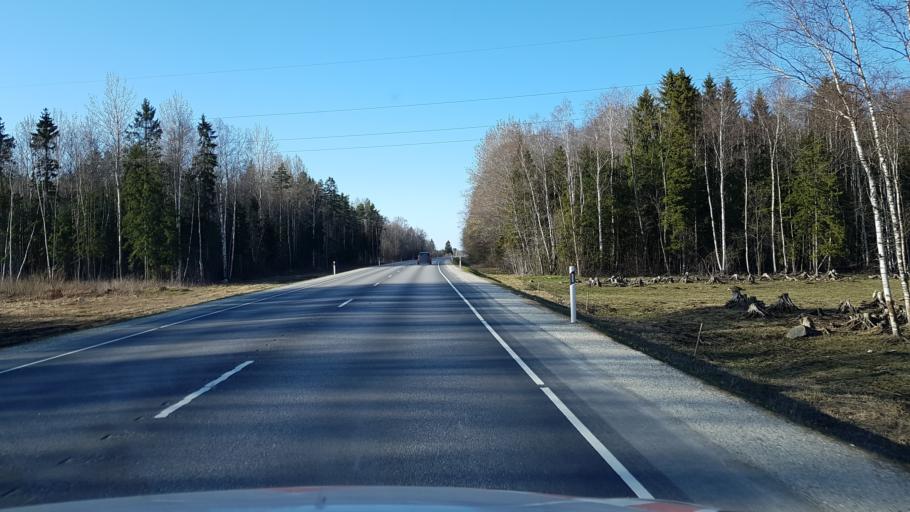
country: EE
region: Ida-Virumaa
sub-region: Johvi vald
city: Johvi
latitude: 59.3044
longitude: 27.3941
